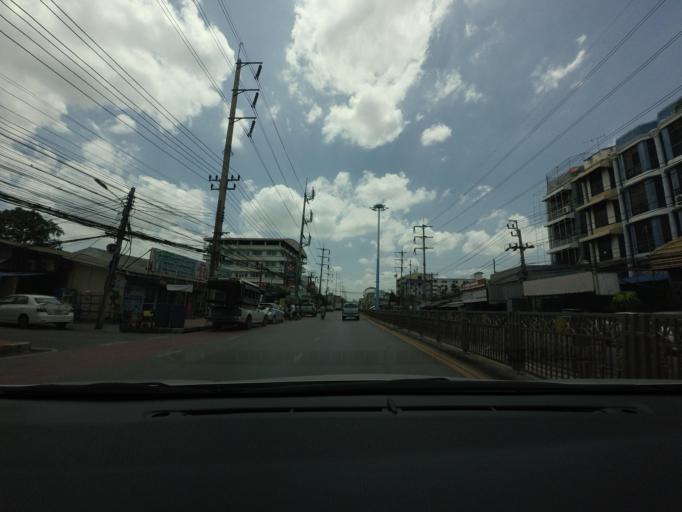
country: TH
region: Samut Prakan
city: Samut Prakan
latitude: 13.5744
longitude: 100.5919
